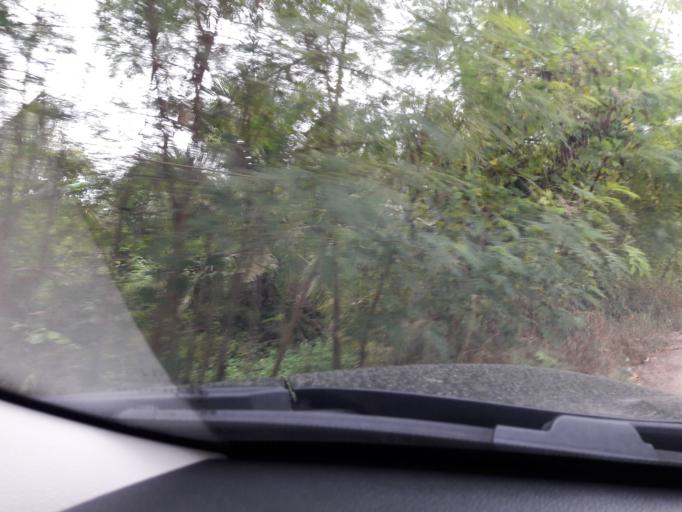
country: TH
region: Ratchaburi
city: Bang Phae
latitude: 13.6152
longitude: 99.9672
